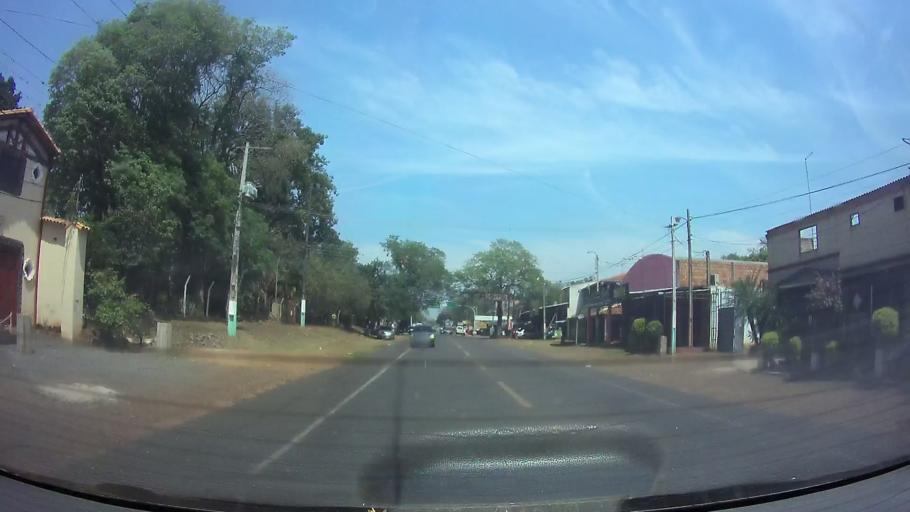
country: PY
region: Central
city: Guarambare
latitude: -25.4294
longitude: -57.4502
